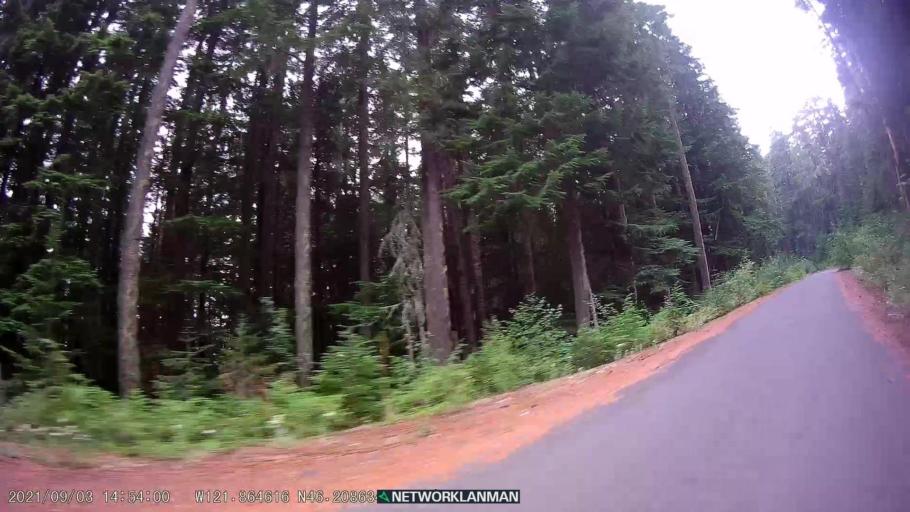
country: US
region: Washington
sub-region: Skamania County
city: Carson
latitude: 46.2087
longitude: -121.8648
